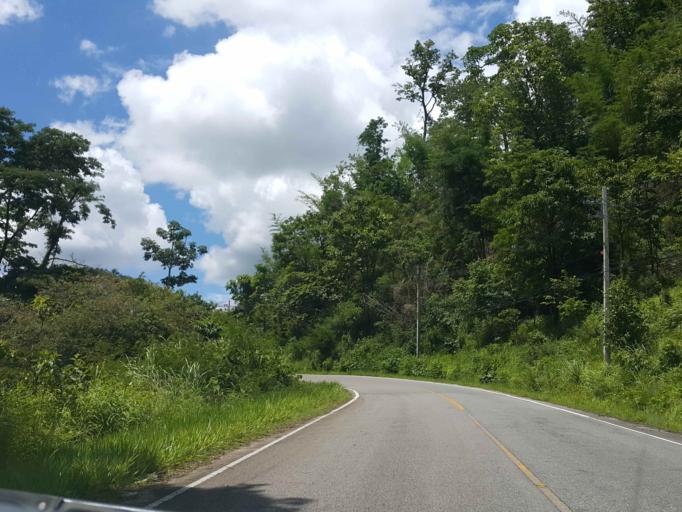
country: TH
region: Chiang Mai
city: Samoeng
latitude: 18.8660
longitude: 98.7798
